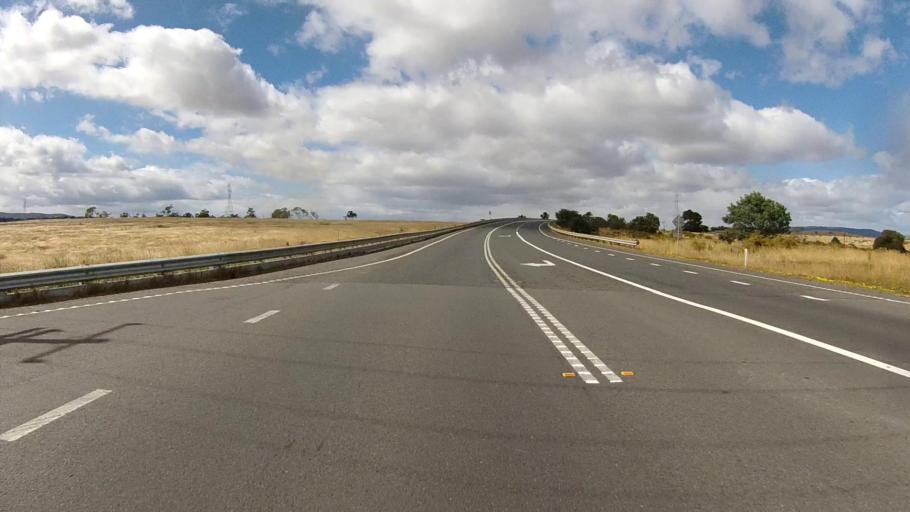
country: AU
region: Tasmania
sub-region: Northern Midlands
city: Evandale
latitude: -41.8359
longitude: 147.4473
